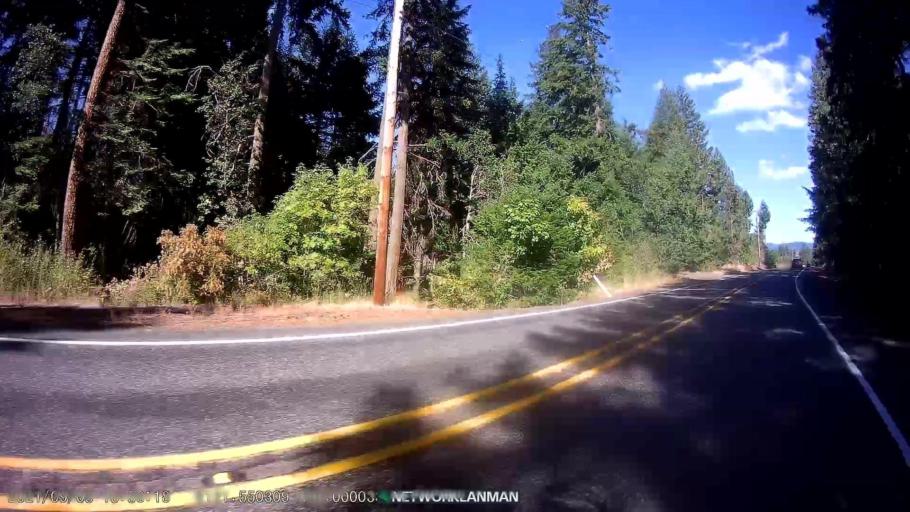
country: US
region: Washington
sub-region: Klickitat County
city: White Salmon
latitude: 46.0002
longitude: -121.5499
